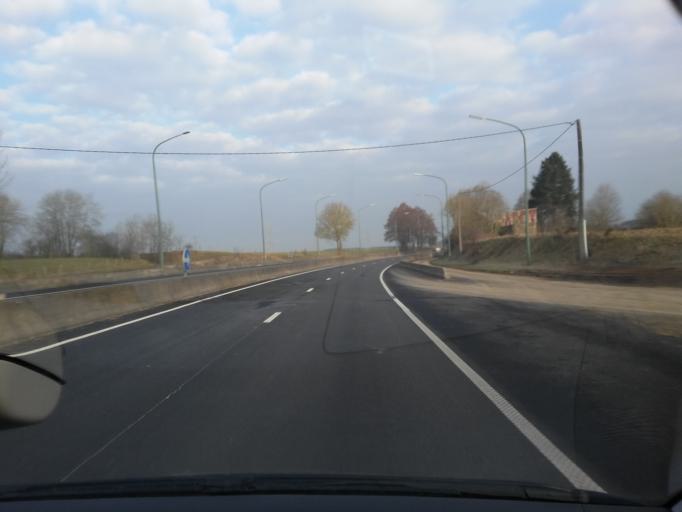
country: BE
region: Wallonia
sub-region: Province du Luxembourg
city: Martelange
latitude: 49.8662
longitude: 5.7146
